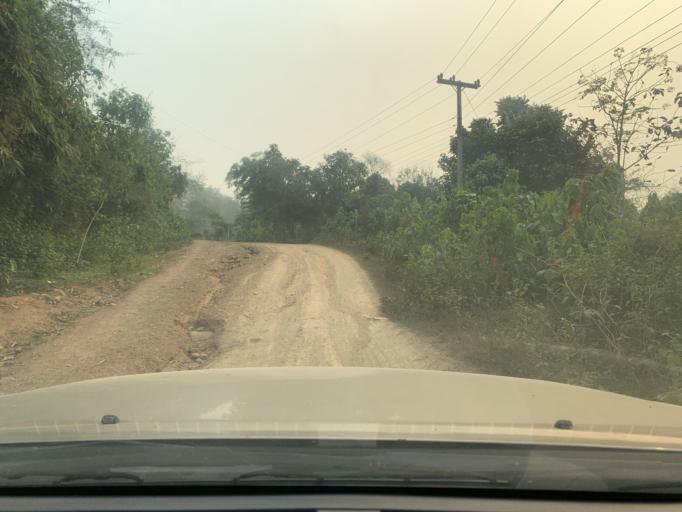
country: LA
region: Louangphabang
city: Louangphabang
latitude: 19.9284
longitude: 102.0777
